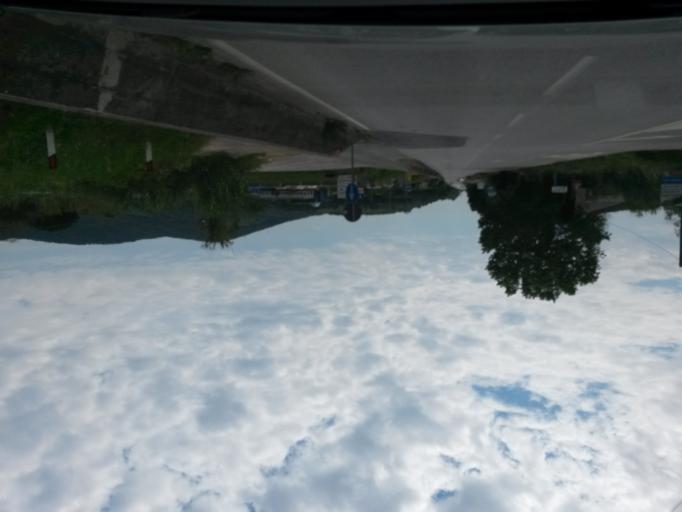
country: IT
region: Tuscany
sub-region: Provincia di Livorno
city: Piombino
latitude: 42.9622
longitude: 10.5368
